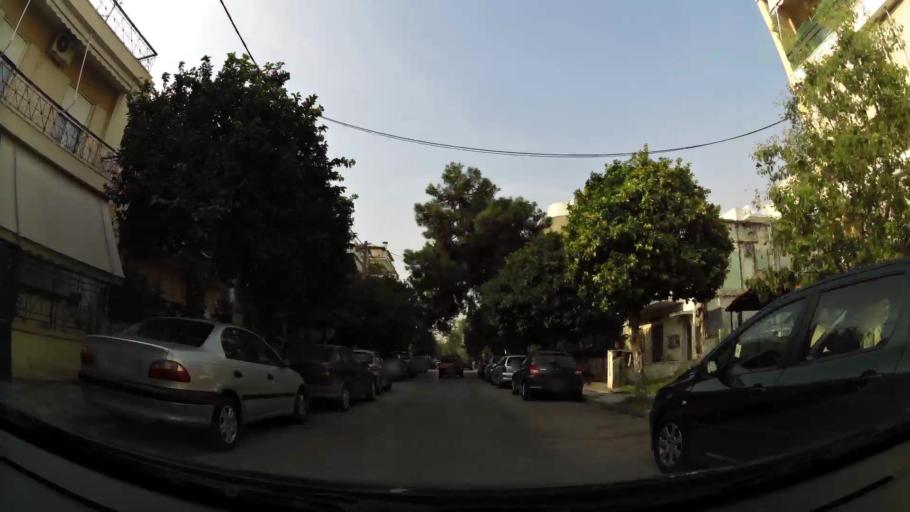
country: GR
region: Attica
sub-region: Nomarchia Athinas
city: Kallithea
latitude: 37.9532
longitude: 23.6927
